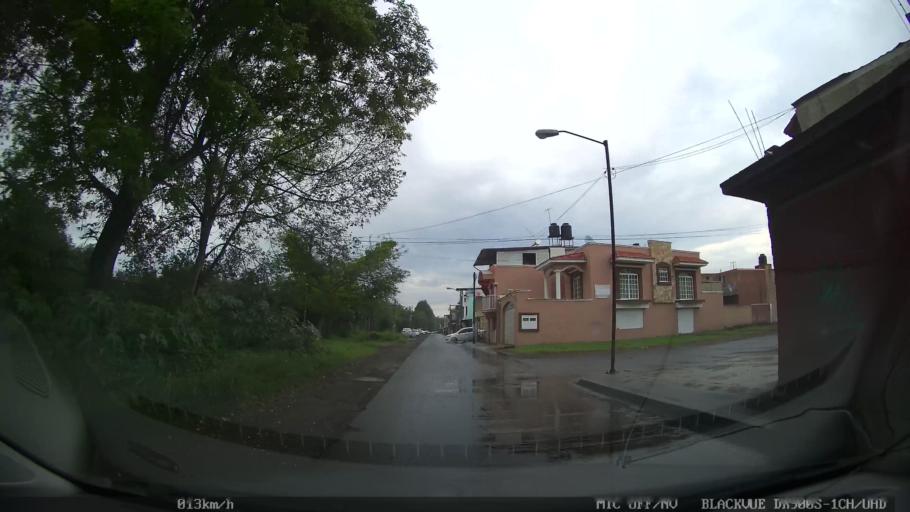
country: MX
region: Michoacan
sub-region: Uruapan
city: Santa Rosa (Santa Barbara)
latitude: 19.4002
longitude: -102.0275
